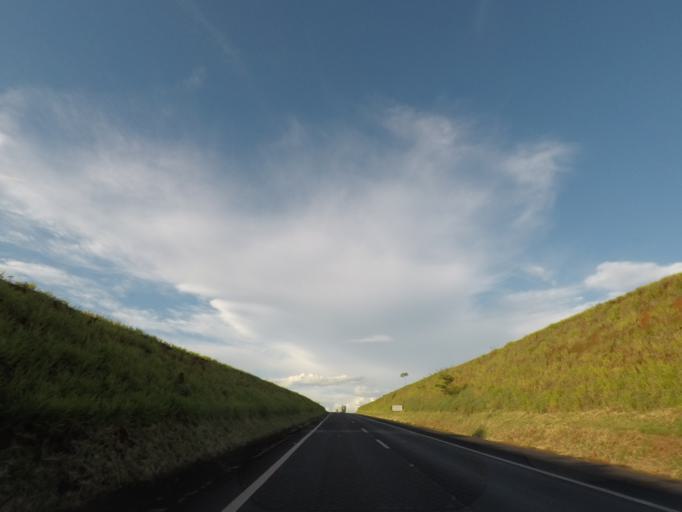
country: BR
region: Sao Paulo
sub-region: Ituverava
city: Ituverava
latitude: -20.2488
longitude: -47.7987
